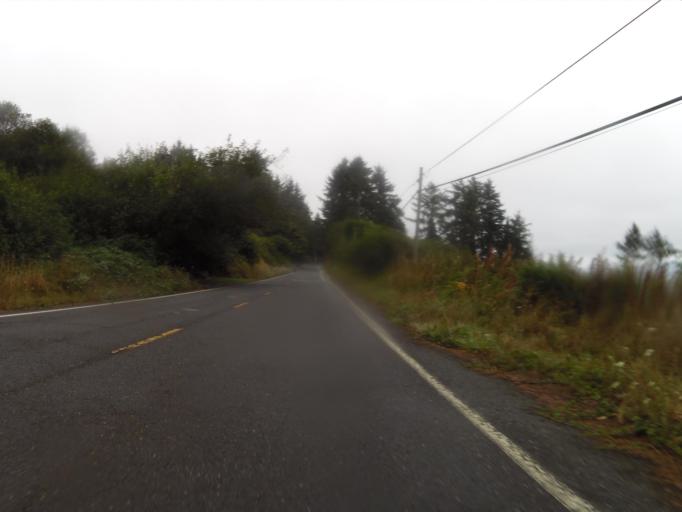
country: US
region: California
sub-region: Humboldt County
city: Westhaven-Moonstone
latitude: 41.1111
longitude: -124.1572
